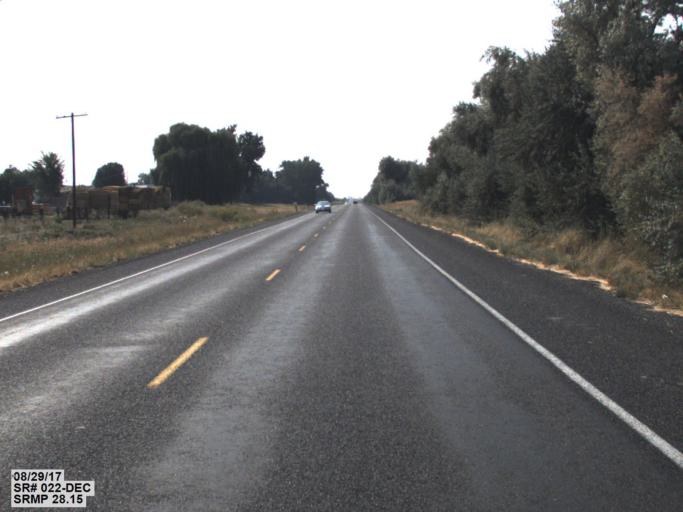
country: US
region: Washington
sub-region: Yakima County
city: Grandview
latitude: 46.1899
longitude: -119.8998
